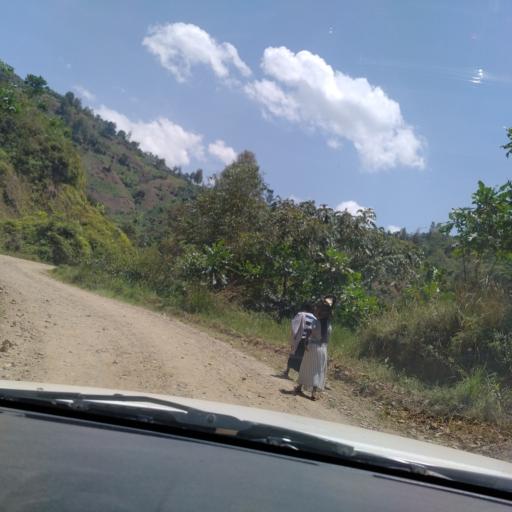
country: CD
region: Nord Kivu
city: Sake
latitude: -1.9672
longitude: 28.9150
